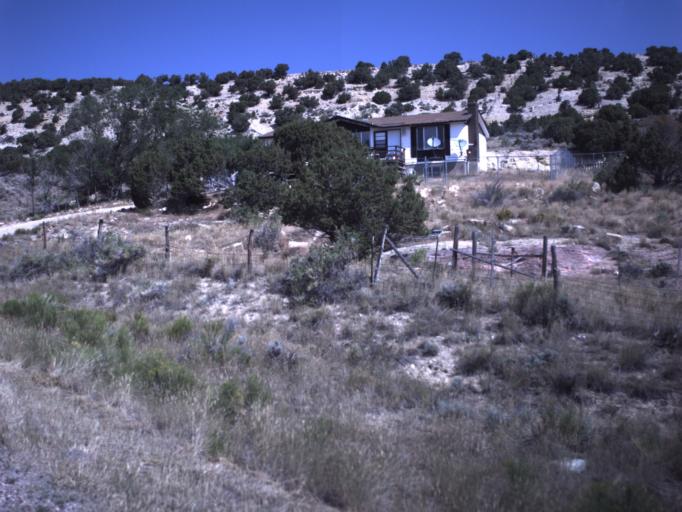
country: US
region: Utah
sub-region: Daggett County
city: Manila
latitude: 40.9779
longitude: -109.7796
